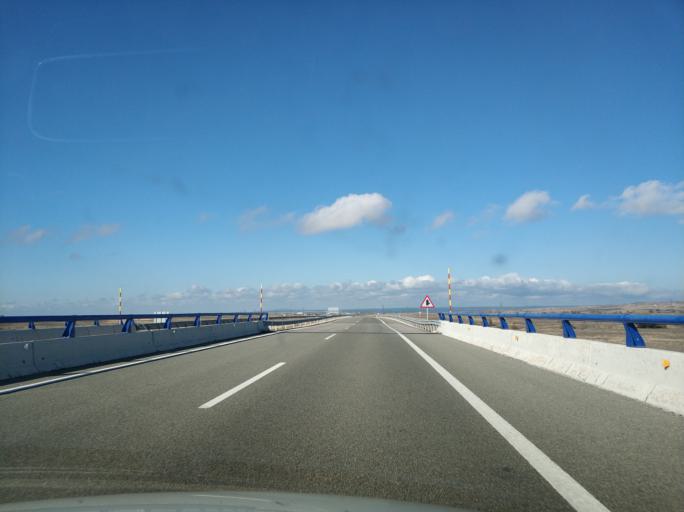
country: ES
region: Castille and Leon
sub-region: Provincia de Soria
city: Coscurita
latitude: 41.4197
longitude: -2.4889
